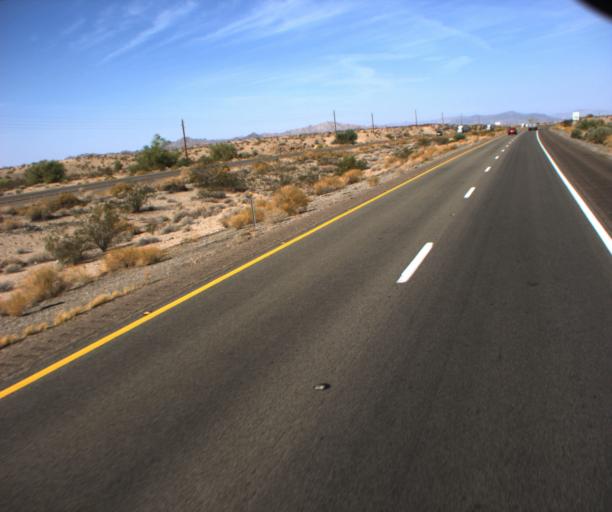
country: US
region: Arizona
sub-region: Mohave County
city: Desert Hills
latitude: 34.7319
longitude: -114.2699
